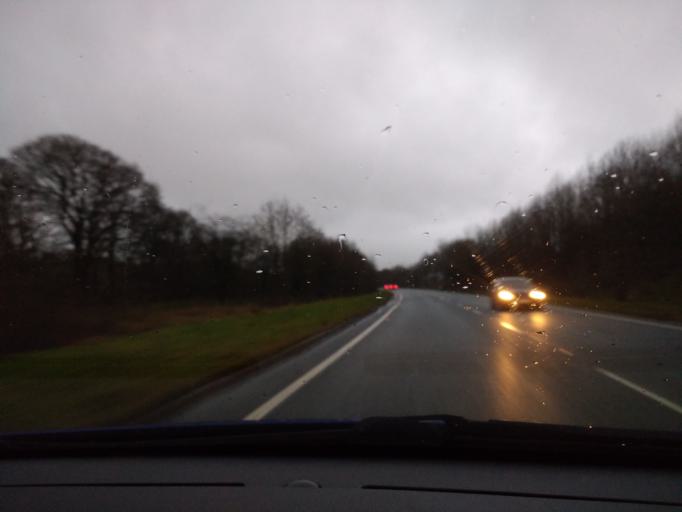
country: GB
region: England
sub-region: Cumbria
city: Cockermouth
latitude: 54.6585
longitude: -3.3212
